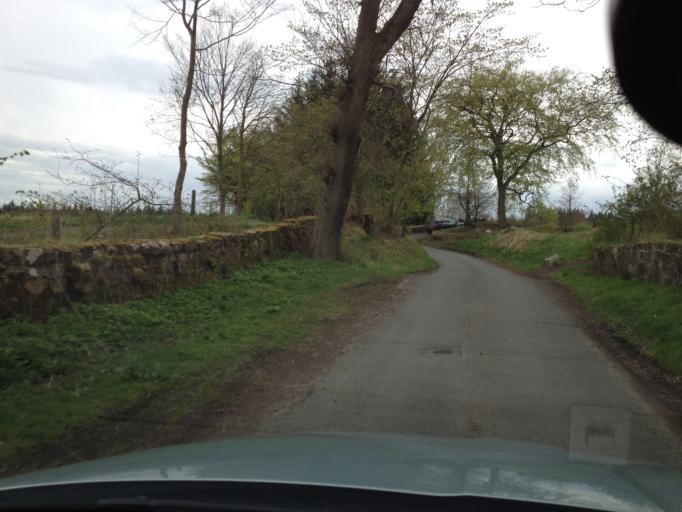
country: GB
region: Scotland
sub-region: West Lothian
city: Linlithgow
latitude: 55.9495
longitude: -3.6054
